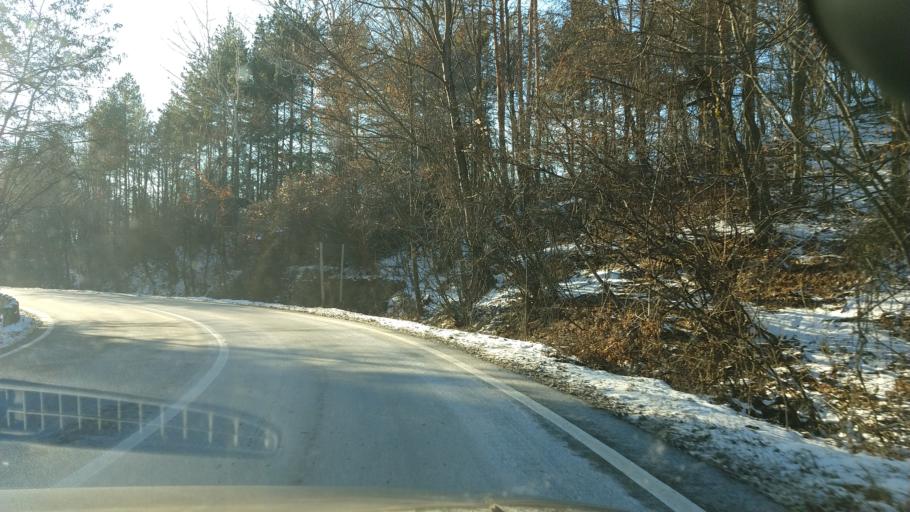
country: RO
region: Bacau
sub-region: Comuna Luizi-Calugara
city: Luizi-Calugara
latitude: 46.4996
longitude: 26.8042
